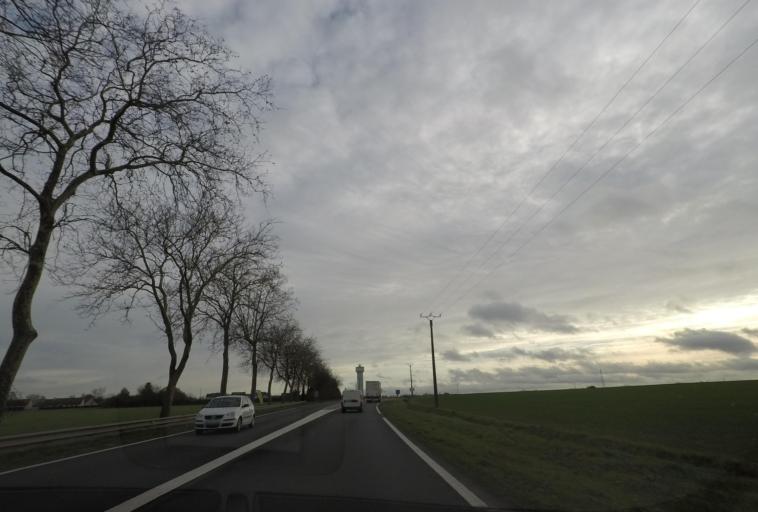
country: FR
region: Centre
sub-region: Departement du Loir-et-Cher
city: Sarge-sur-Braye
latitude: 47.9014
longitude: 0.9195
